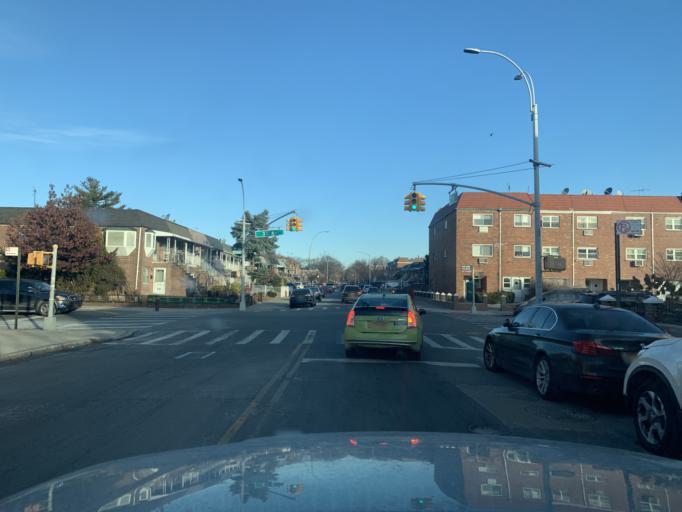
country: US
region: New York
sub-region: Queens County
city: Long Island City
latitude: 40.7605
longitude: -73.8910
